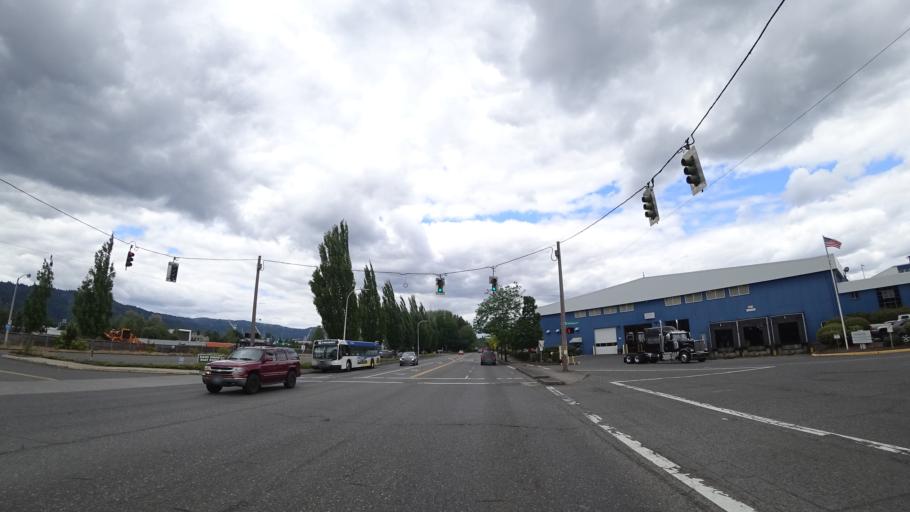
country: US
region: Oregon
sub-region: Multnomah County
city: Portland
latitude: 45.5619
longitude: -122.7037
